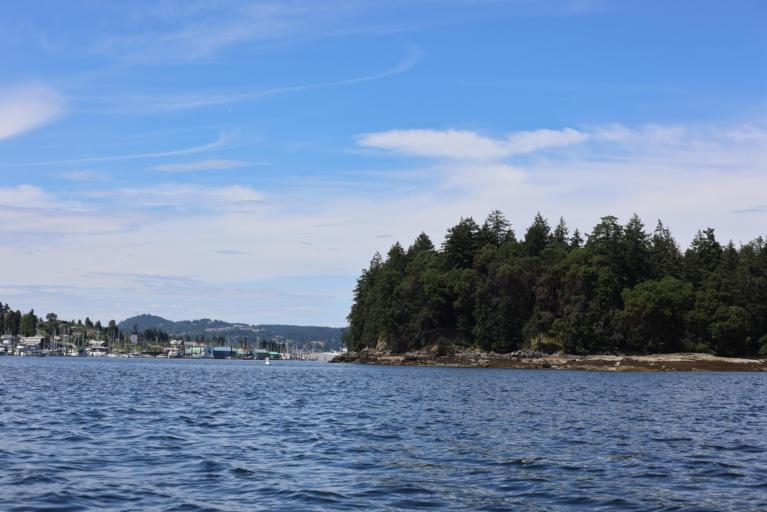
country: CA
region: British Columbia
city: Nanaimo
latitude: 49.1761
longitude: -123.9345
